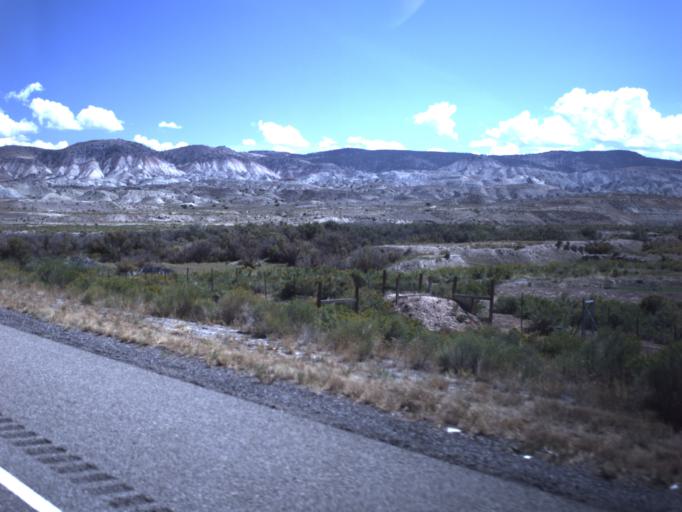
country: US
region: Utah
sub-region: Sevier County
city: Aurora
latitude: 38.9119
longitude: -111.8886
